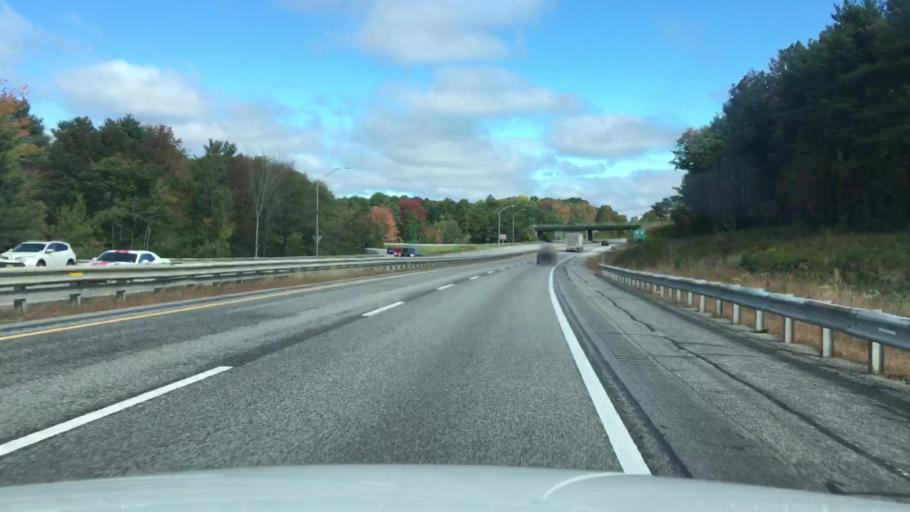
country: US
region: Maine
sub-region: Cumberland County
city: Freeport
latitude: 43.8617
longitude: -70.1098
